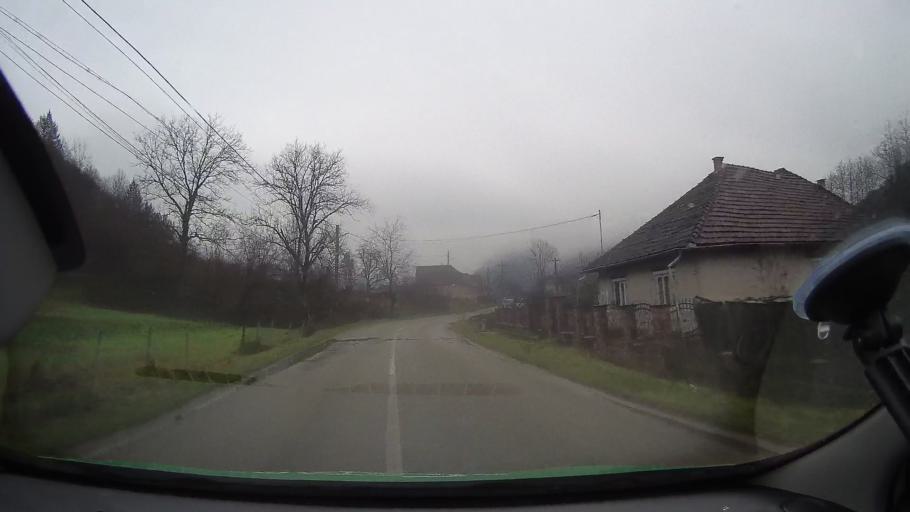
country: RO
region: Arad
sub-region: Comuna Moneasa
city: Moneasa
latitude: 46.4285
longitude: 22.2545
